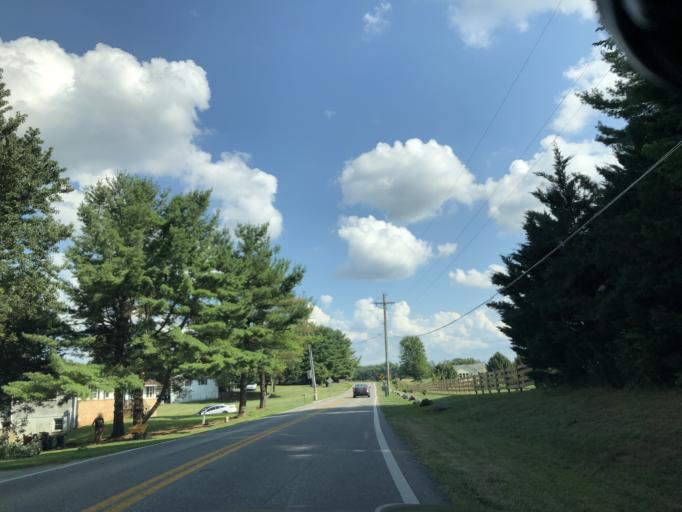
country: US
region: Maryland
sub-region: Frederick County
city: Linganore
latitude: 39.4143
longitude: -77.2071
